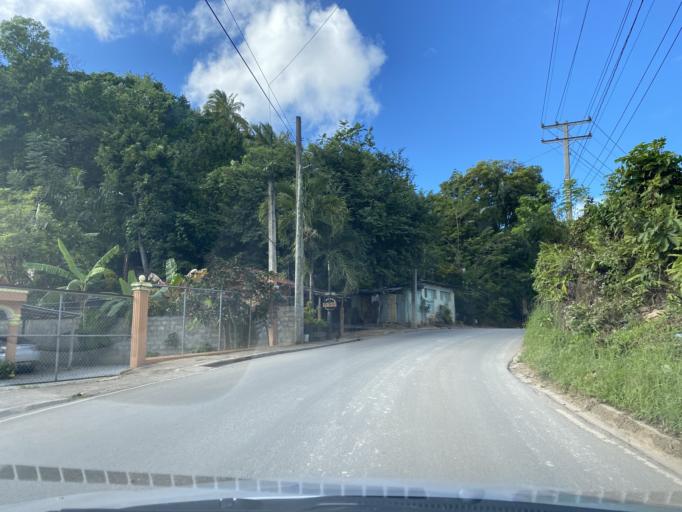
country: DO
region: Samana
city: Las Terrenas
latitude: 19.2975
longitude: -69.5521
